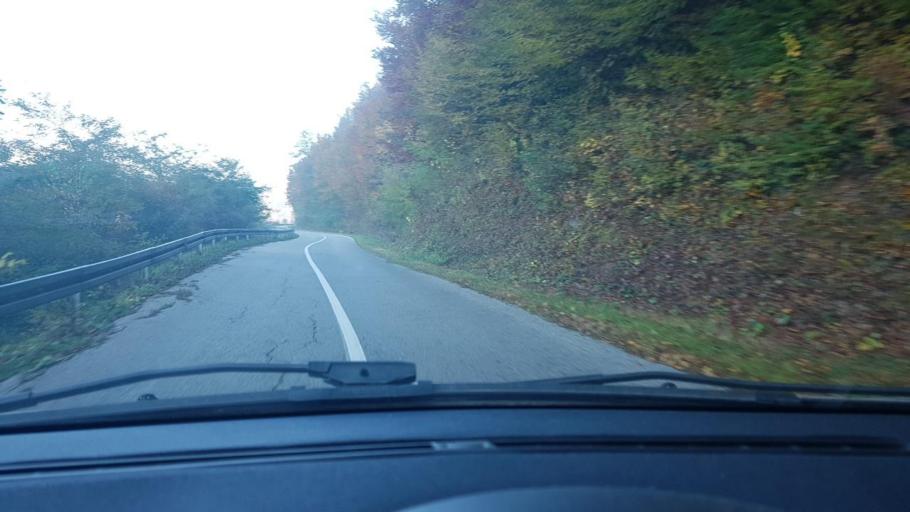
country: SI
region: Podcetrtek
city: Podcetrtek
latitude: 46.1712
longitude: 15.6211
